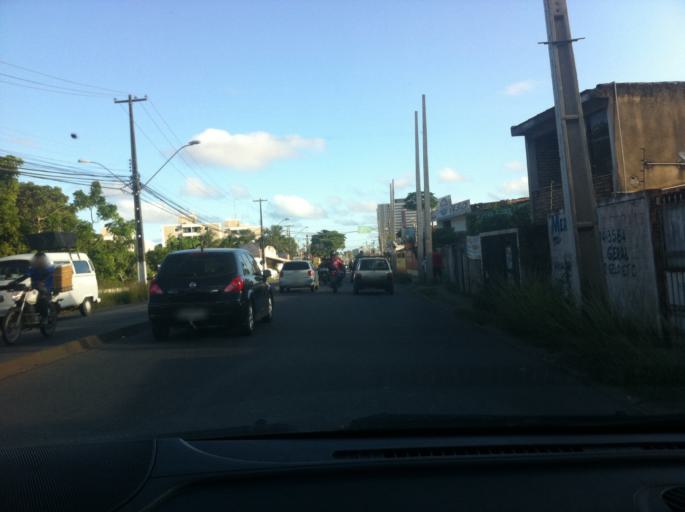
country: BR
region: Alagoas
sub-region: Maceio
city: Maceio
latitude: -9.5972
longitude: -35.7235
